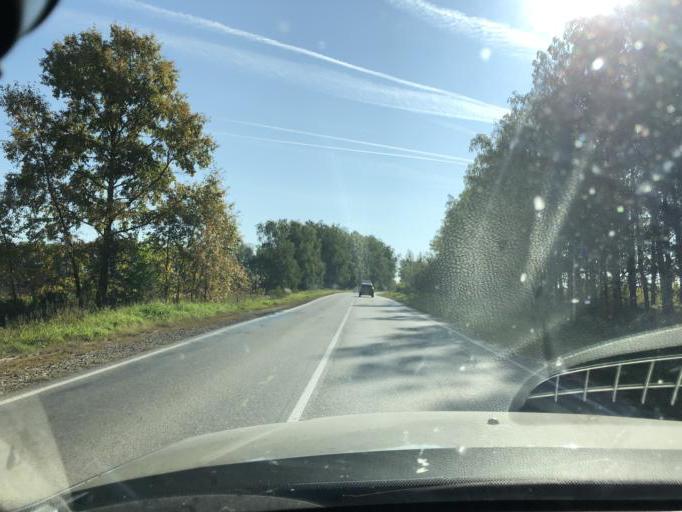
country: RU
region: Tula
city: Yasnogorsk
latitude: 54.4696
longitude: 37.5943
